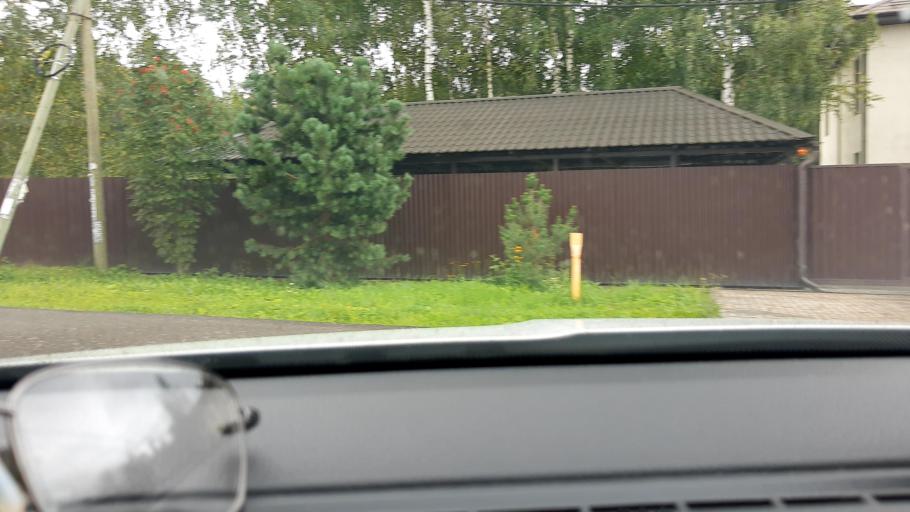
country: RU
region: Moskovskaya
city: Dolgoprudnyy
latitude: 55.9446
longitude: 37.4568
